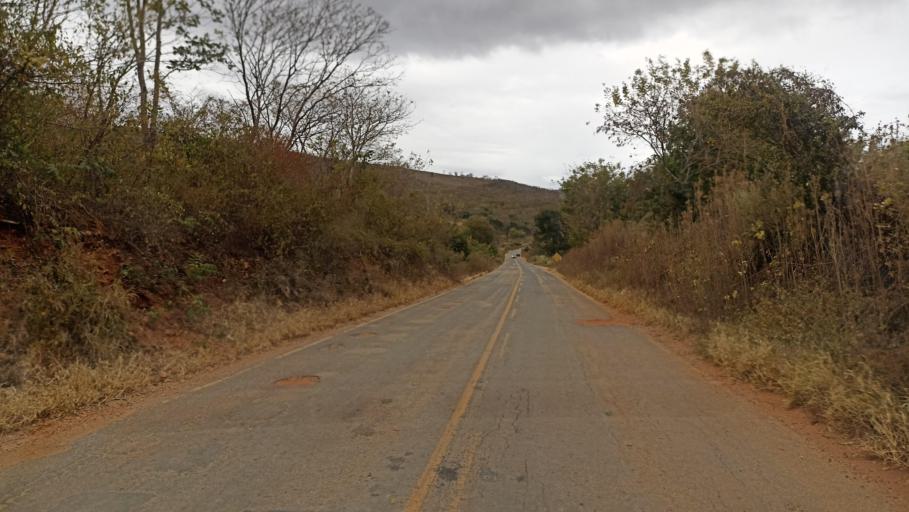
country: BR
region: Minas Gerais
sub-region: Itinga
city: Itinga
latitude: -16.6490
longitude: -41.8297
